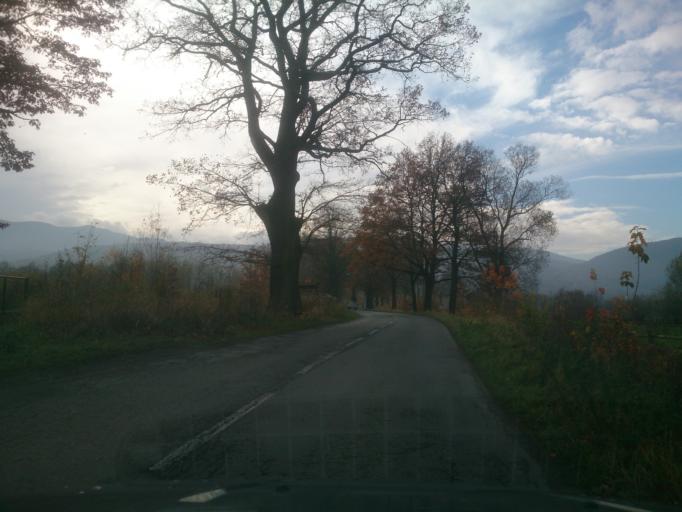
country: PL
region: Lower Silesian Voivodeship
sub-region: Powiat jeleniogorski
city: Podgorzyn
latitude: 50.8417
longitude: 15.6826
